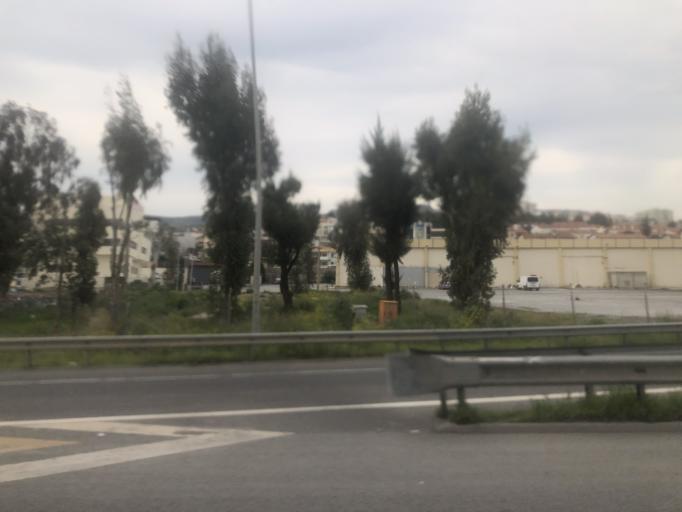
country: TR
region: Izmir
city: Karsiyaka
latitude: 38.4862
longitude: 27.0786
